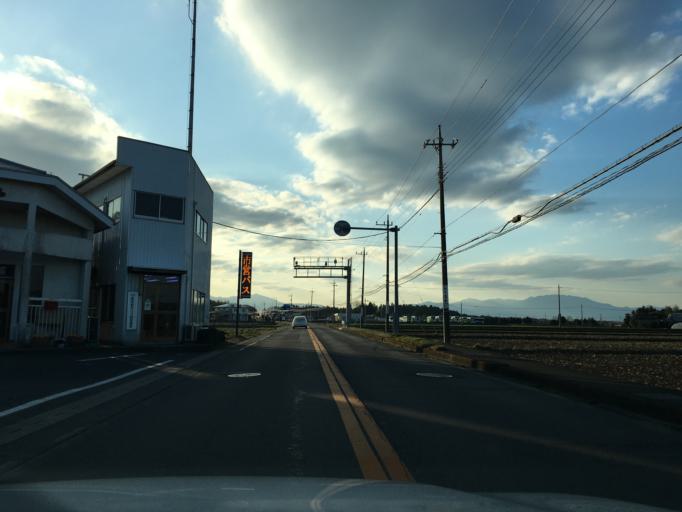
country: JP
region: Tochigi
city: Otawara
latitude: 36.8587
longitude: 140.0993
